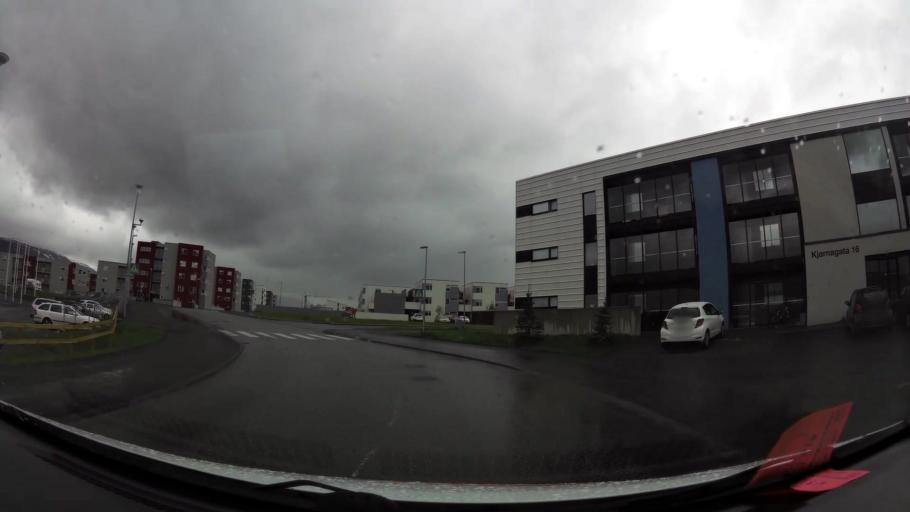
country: IS
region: Northeast
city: Akureyri
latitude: 65.6647
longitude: -18.1010
